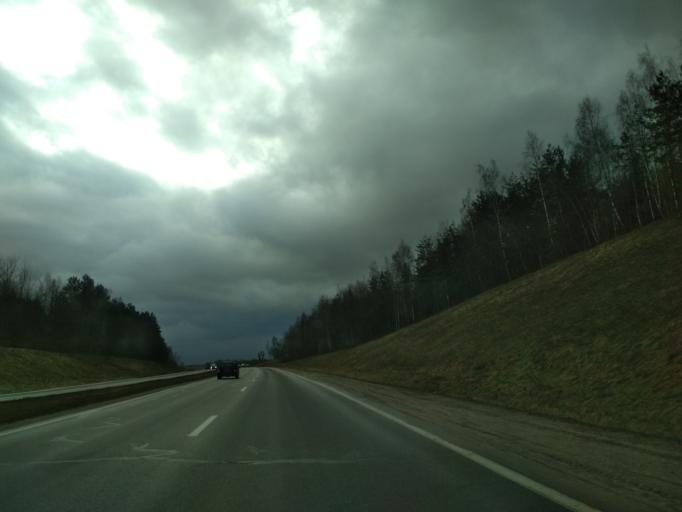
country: BY
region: Minsk
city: Luhavaya Slabada
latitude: 53.7670
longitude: 27.8274
